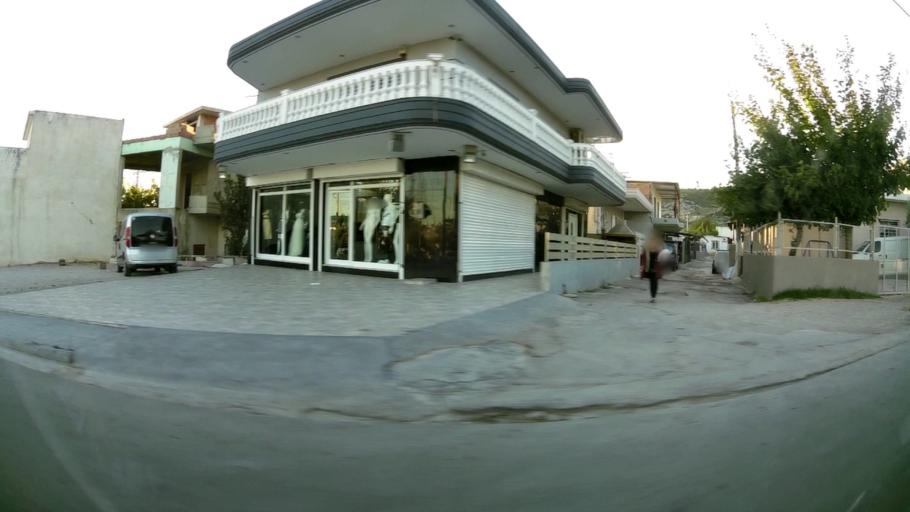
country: GR
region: Attica
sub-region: Nomarchia Dytikis Attikis
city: Ano Liosia
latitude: 38.0908
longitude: 23.6893
